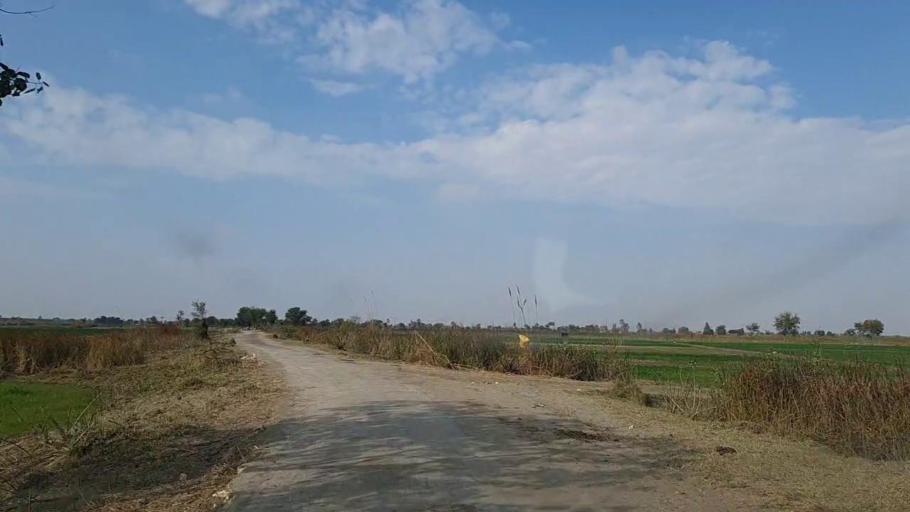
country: PK
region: Sindh
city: Sanghar
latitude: 26.2519
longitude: 69.0123
